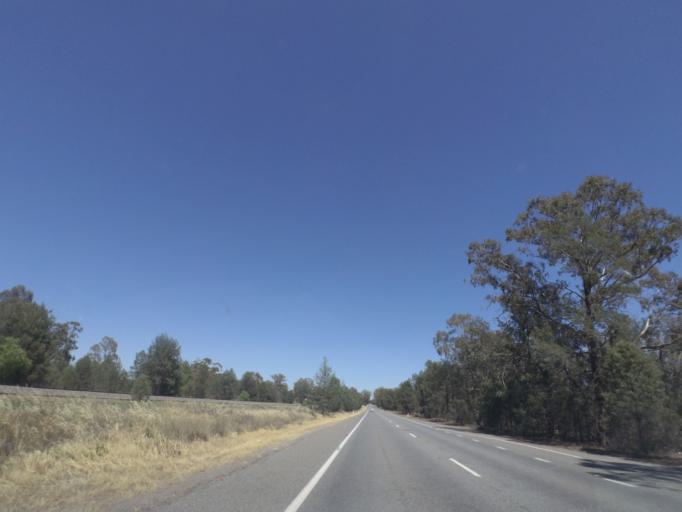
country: AU
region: New South Wales
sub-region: Narrandera
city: Narrandera
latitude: -34.7372
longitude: 146.5884
